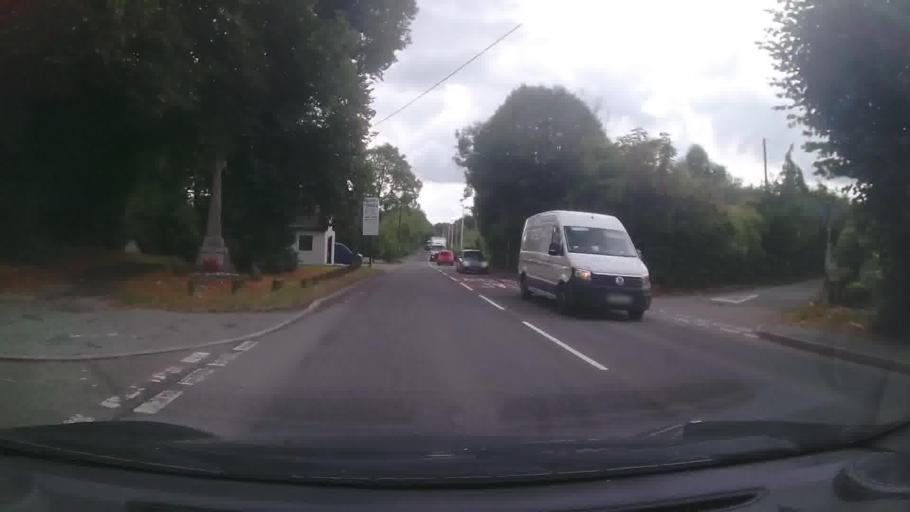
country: GB
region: England
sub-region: Shropshire
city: Pant
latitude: 52.7800
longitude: -3.0882
